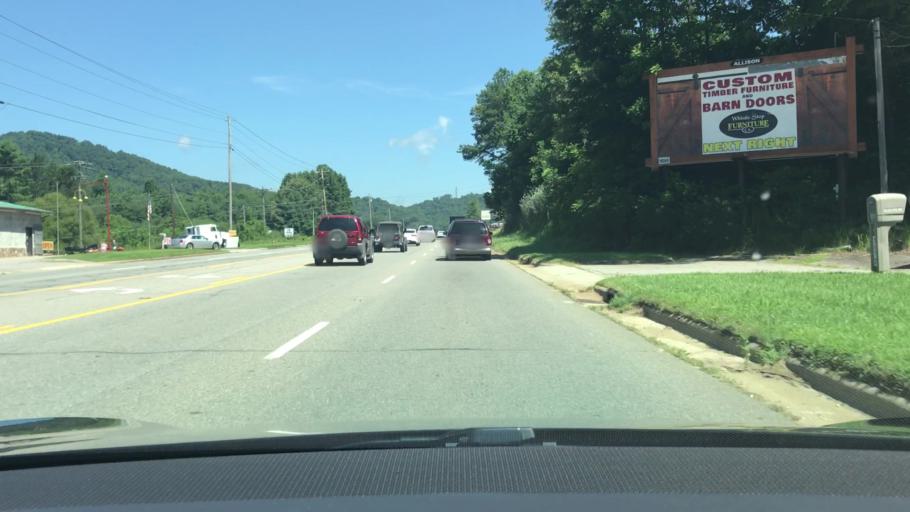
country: US
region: North Carolina
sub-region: Macon County
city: Franklin
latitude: 35.1243
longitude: -83.3939
